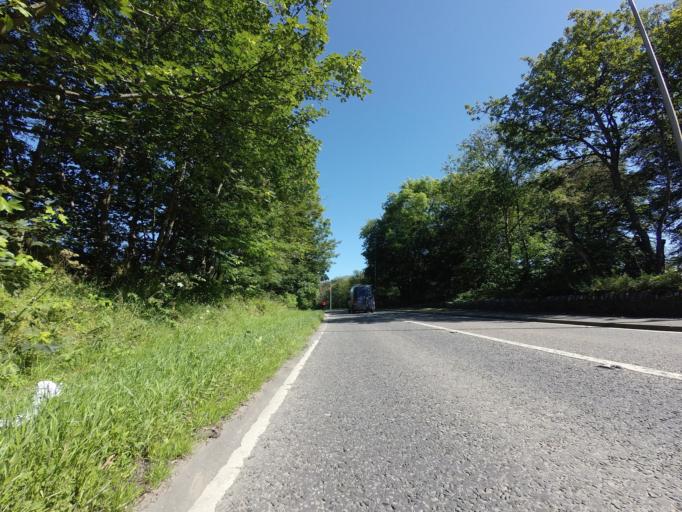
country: GB
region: Scotland
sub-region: Aberdeenshire
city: Macduff
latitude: 57.6589
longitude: -2.5096
